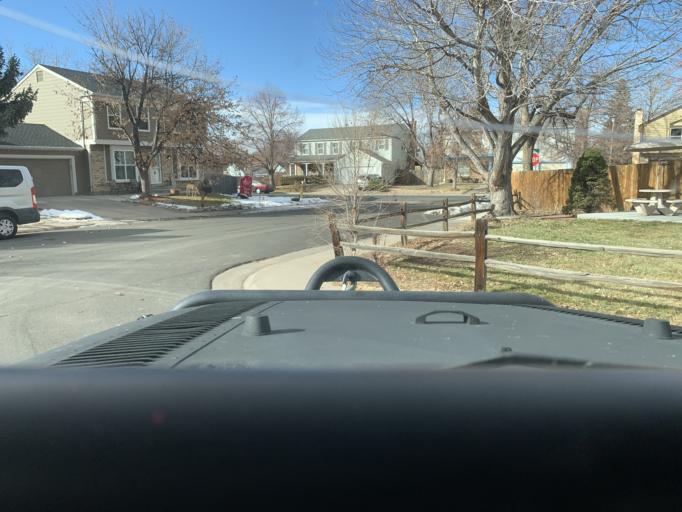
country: US
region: Colorado
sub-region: Adams County
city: Aurora
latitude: 39.7029
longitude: -104.7986
